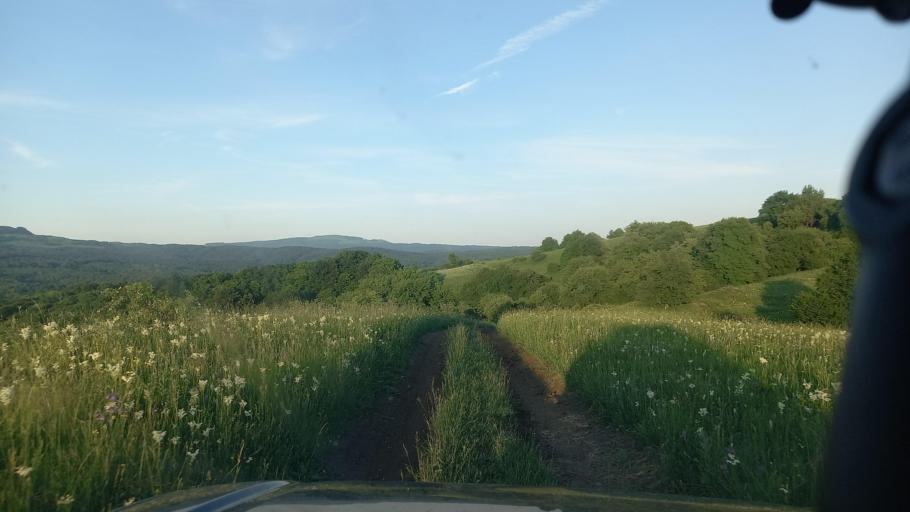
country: RU
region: Karachayevo-Cherkesiya
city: Kurdzhinovo
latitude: 44.1243
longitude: 41.0905
